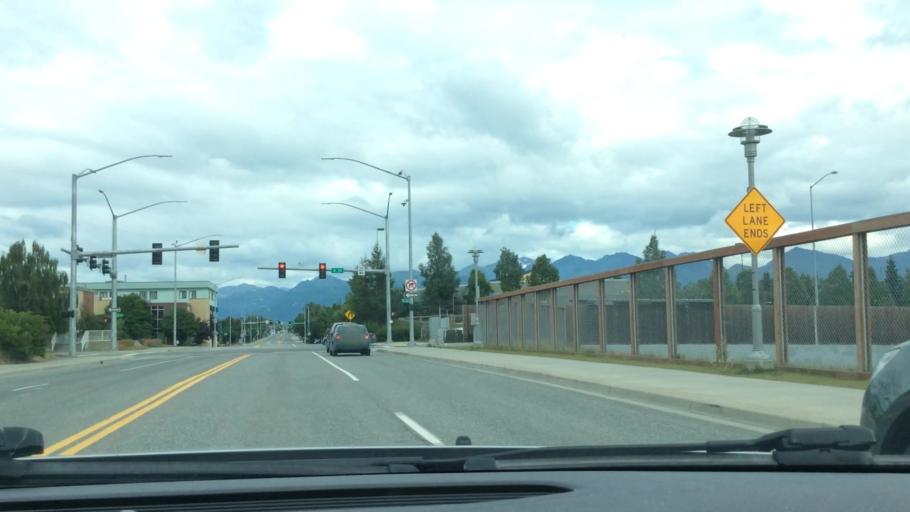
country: US
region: Alaska
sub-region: Anchorage Municipality
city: Anchorage
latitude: 61.2136
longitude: -149.8845
